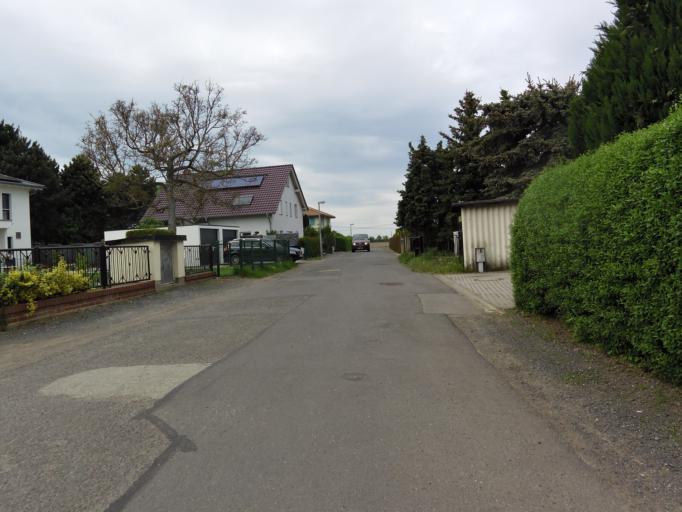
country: DE
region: Saxony
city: Markkleeberg
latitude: 51.2872
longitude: 12.3005
